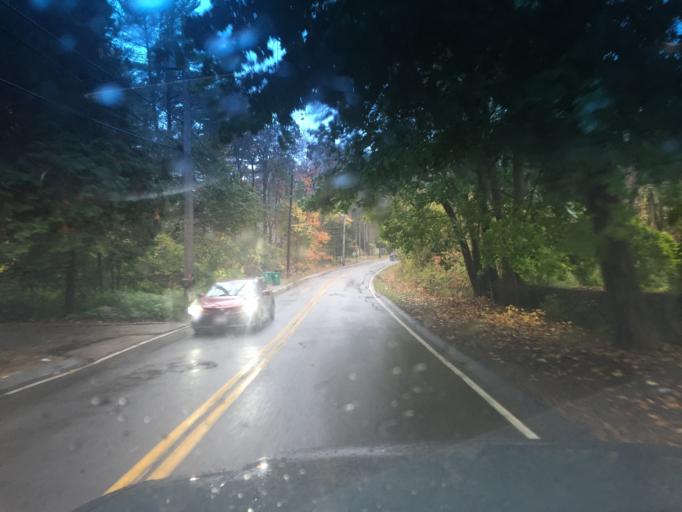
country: US
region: Massachusetts
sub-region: Norfolk County
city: Westwood
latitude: 42.2121
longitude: -71.2145
